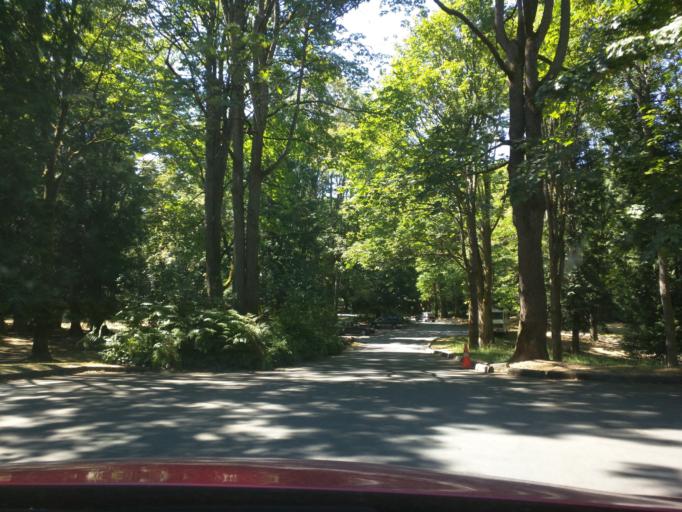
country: US
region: Washington
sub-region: King County
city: Seattle
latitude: 47.6671
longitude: -122.3440
